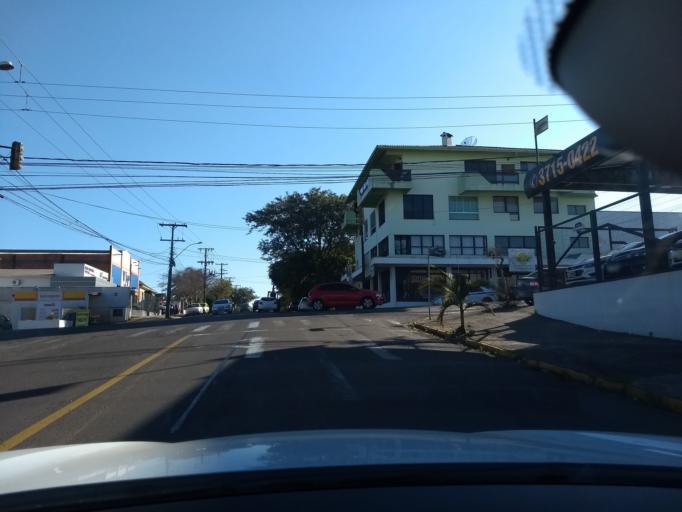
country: BR
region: Rio Grande do Sul
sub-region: Santa Cruz Do Sul
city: Santa Cruz do Sul
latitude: -29.7163
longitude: -52.4415
